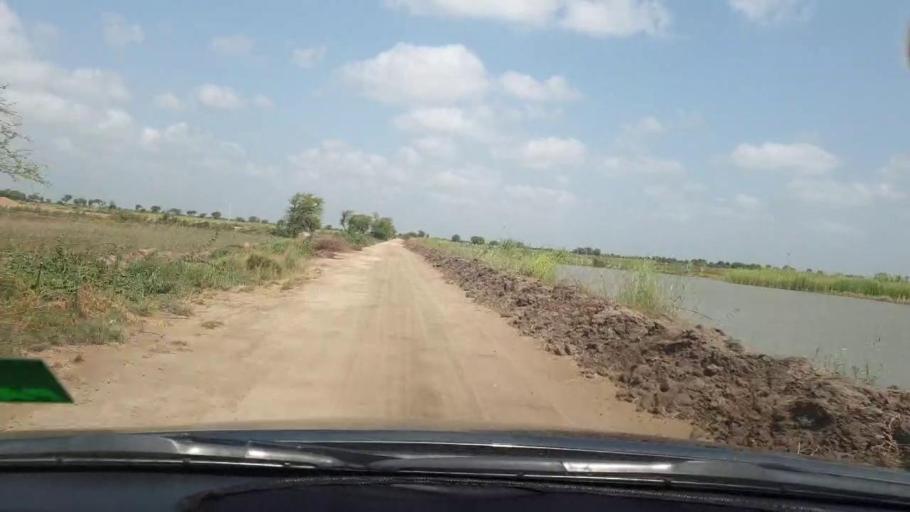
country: PK
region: Sindh
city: Tando Bago
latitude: 24.8610
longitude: 69.0354
